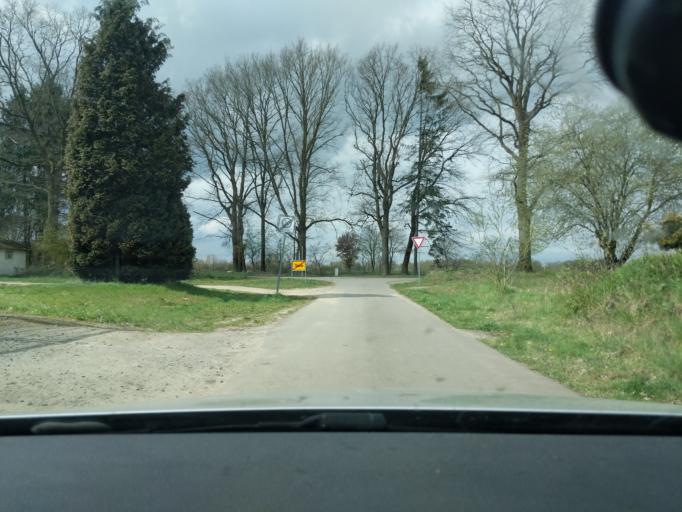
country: DE
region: Lower Saxony
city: Stade
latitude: 53.5700
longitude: 9.4646
